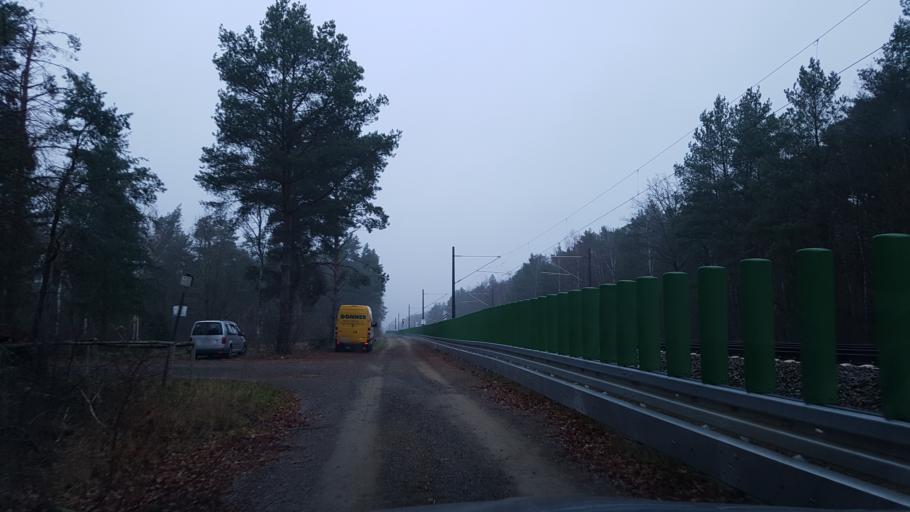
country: DE
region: Brandenburg
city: Ruckersdorf
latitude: 51.5438
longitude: 13.5760
